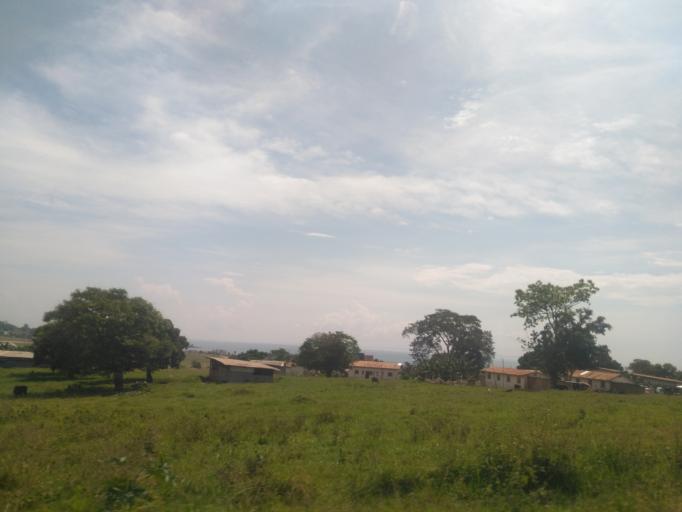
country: UG
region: Central Region
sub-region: Wakiso District
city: Entebbe
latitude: 0.0383
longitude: 32.4476
